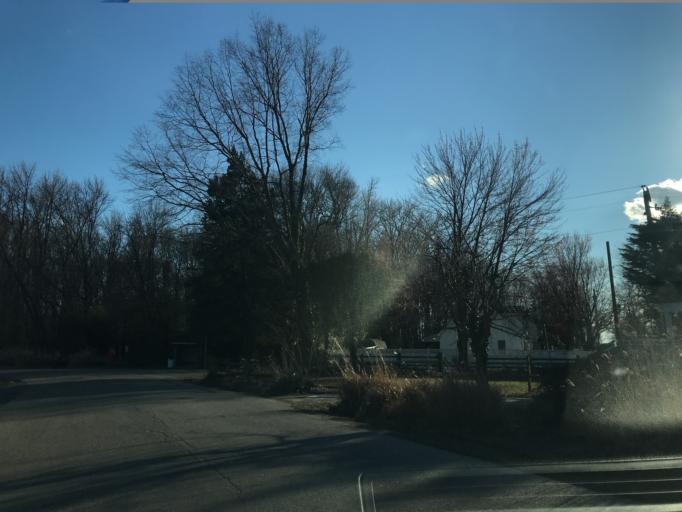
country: US
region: Maryland
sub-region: Anne Arundel County
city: Mayo
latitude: 38.8778
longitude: -76.5106
